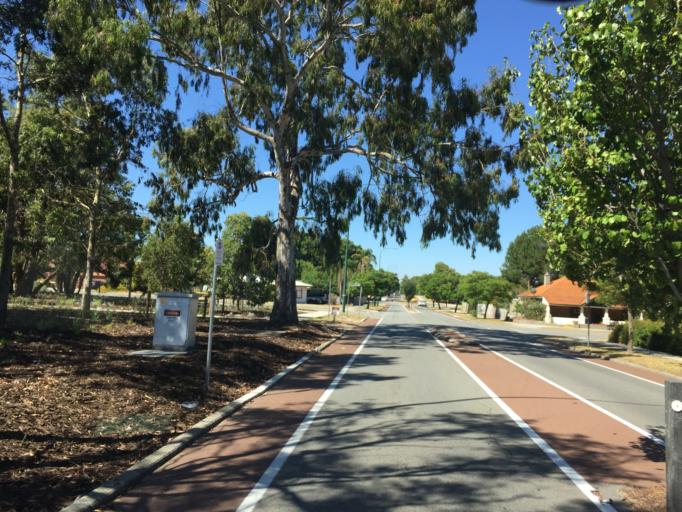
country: AU
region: Western Australia
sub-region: Victoria Park
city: Victoria Park
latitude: -31.9732
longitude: 115.9101
